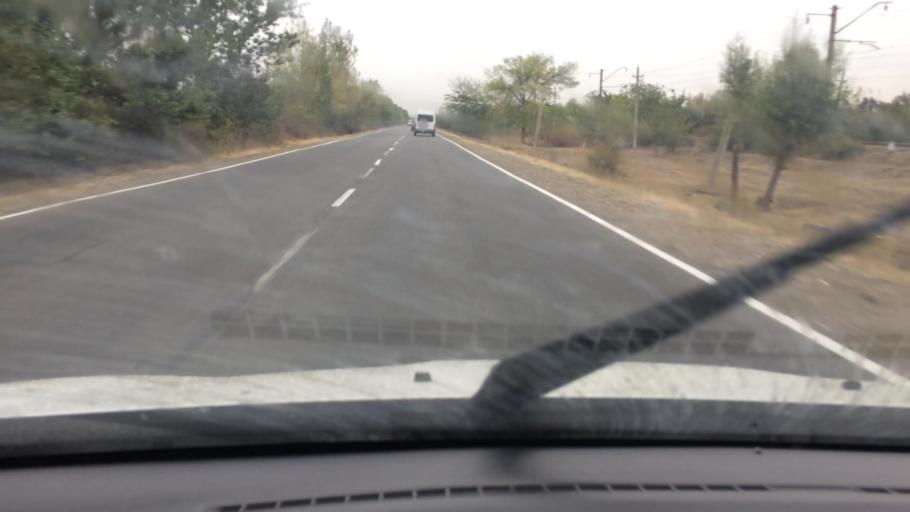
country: GE
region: Kvemo Kartli
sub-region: Marneuli
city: Marneuli
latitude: 41.4445
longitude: 44.8160
